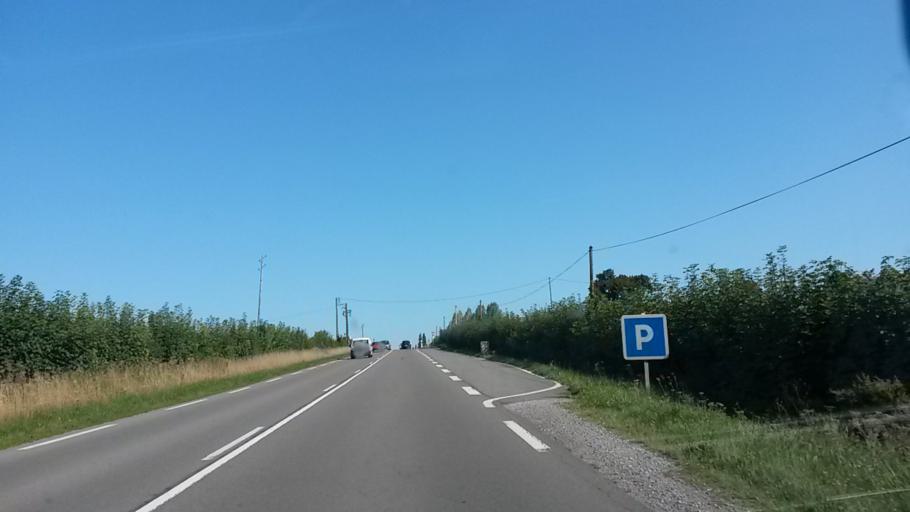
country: FR
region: Nord-Pas-de-Calais
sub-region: Departement du Nord
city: Avesnes-sur-Helpe
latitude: 50.0762
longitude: 3.9292
